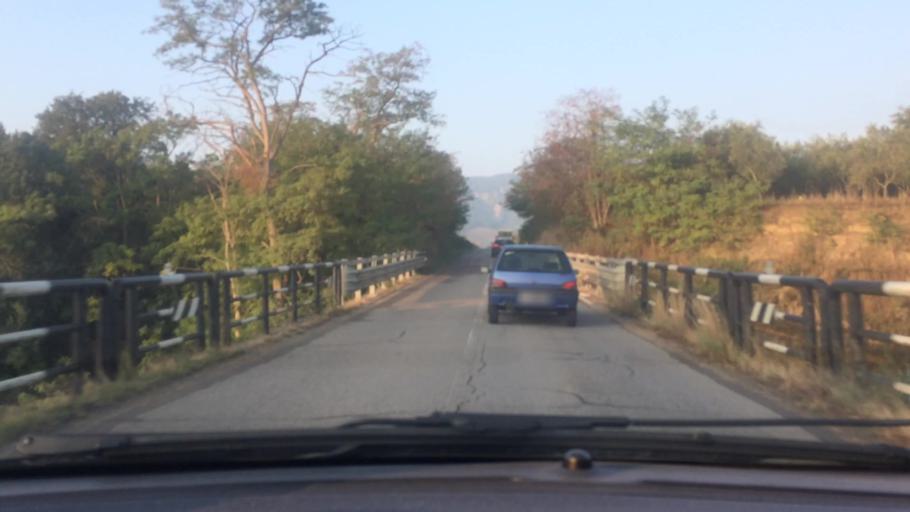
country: IT
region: Basilicate
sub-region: Provincia di Matera
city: Montescaglioso
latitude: 40.5309
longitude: 16.6355
